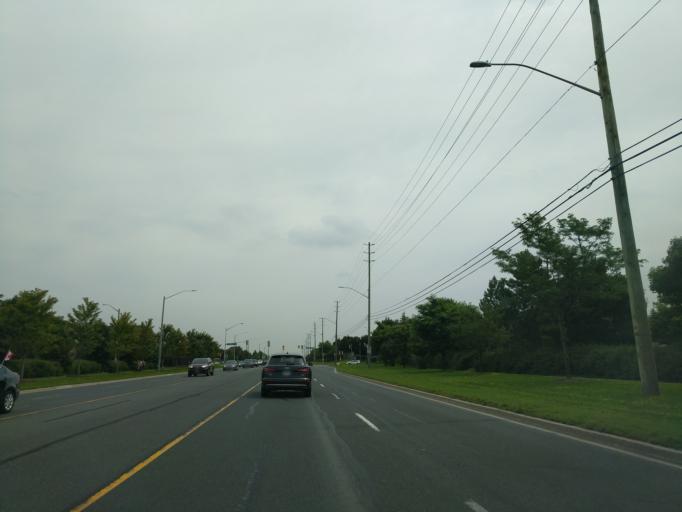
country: CA
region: Ontario
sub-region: York
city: Richmond Hill
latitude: 43.8777
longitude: -79.4024
